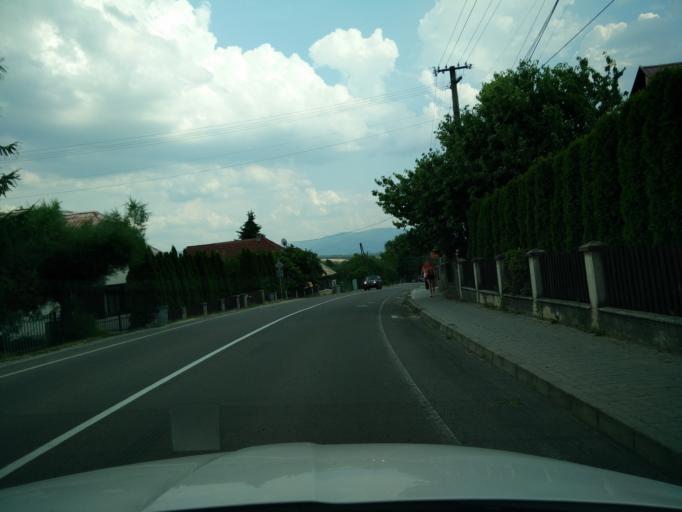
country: SK
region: Nitriansky
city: Novaky
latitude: 48.7668
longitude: 18.4938
